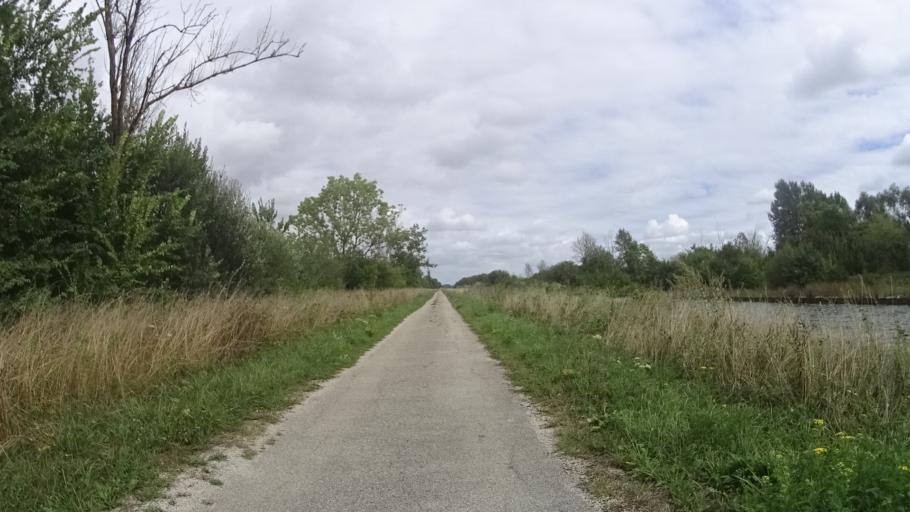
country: FR
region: Picardie
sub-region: Departement de l'Aisne
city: Ognes
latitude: 49.5953
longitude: 3.1952
